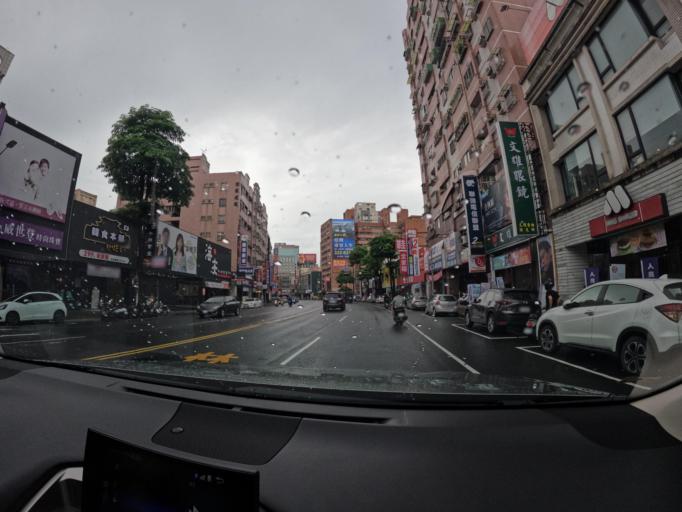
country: TW
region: Kaohsiung
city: Kaohsiung
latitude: 22.6649
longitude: 120.3083
